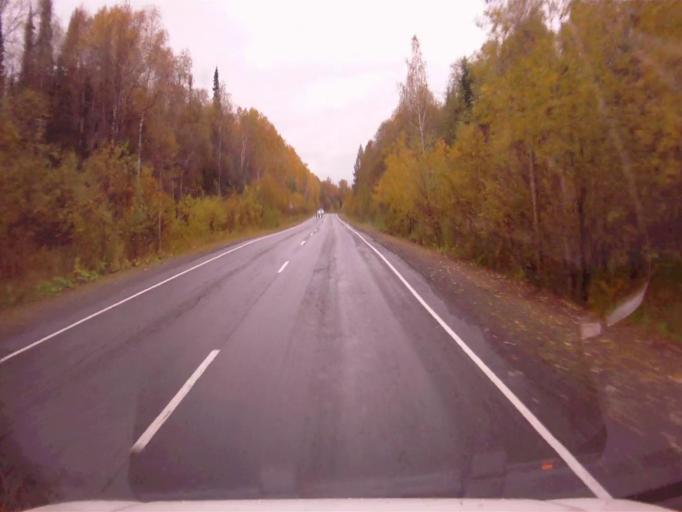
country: RU
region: Chelyabinsk
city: Nizhniy Ufaley
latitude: 56.0637
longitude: 59.9986
